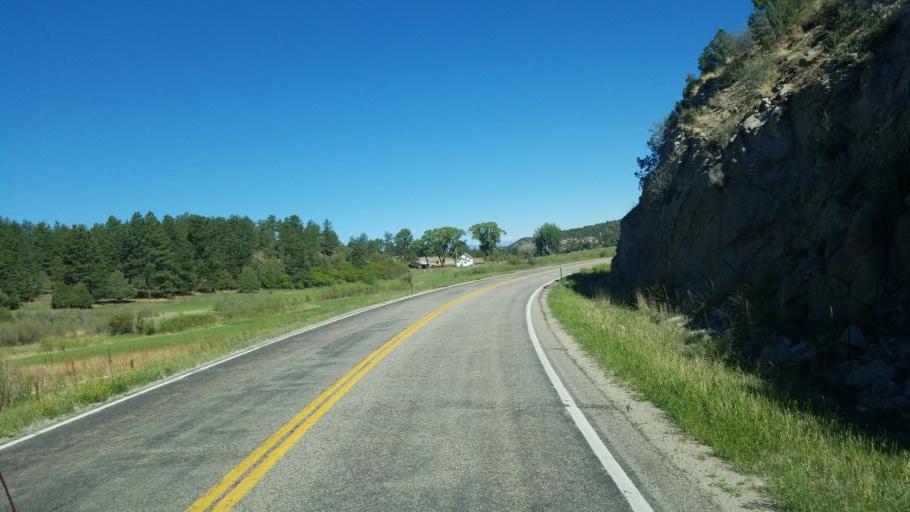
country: US
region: Colorado
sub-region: Custer County
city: Westcliffe
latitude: 38.2384
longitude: -105.5640
